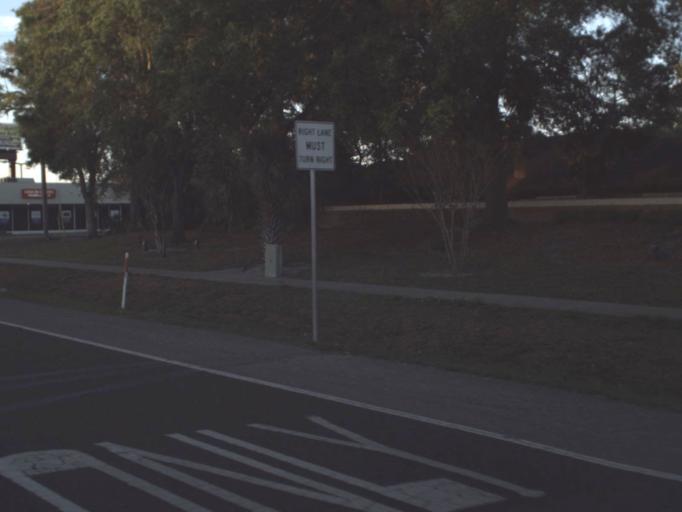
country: US
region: Florida
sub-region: Seminole County
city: Goldenrod
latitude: 28.5893
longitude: -81.3069
